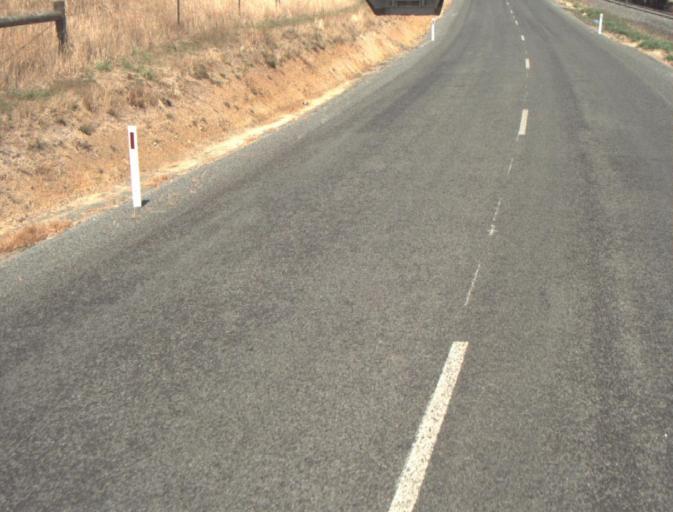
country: AU
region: Tasmania
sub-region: Launceston
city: Newstead
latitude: -41.4747
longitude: 147.1876
